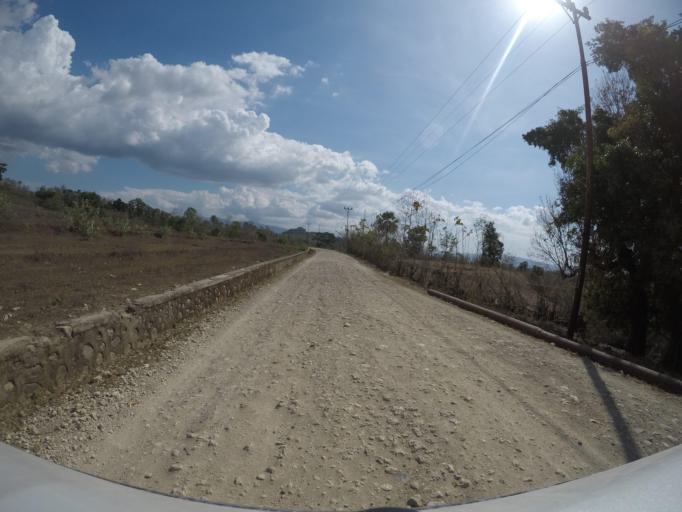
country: TL
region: Bobonaro
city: Maliana
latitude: -8.9955
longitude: 125.2004
